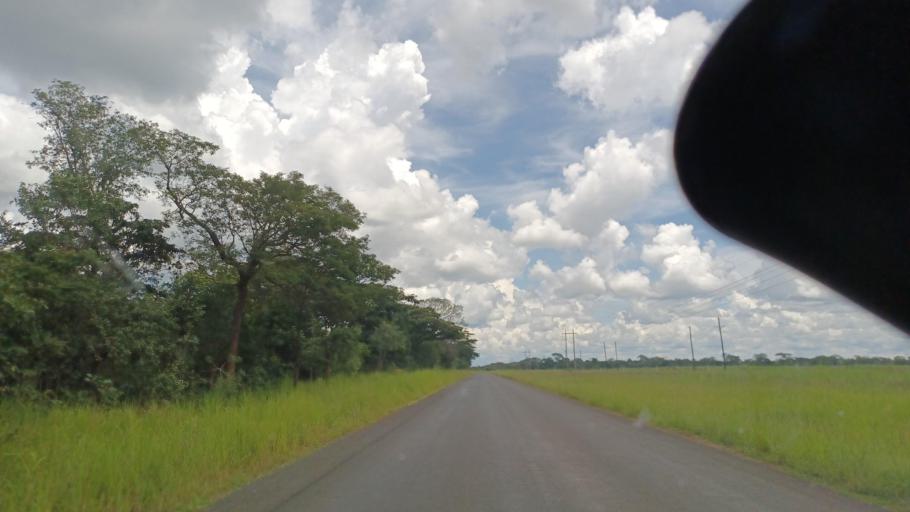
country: ZM
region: North-Western
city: Solwezi
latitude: -12.4537
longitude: 26.2048
